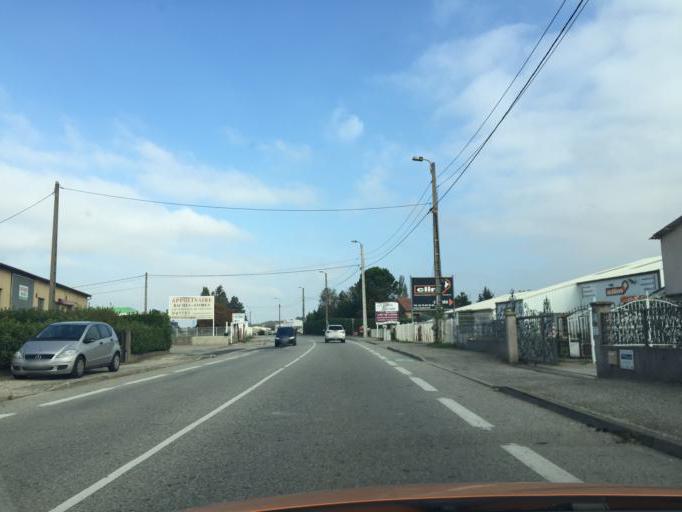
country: FR
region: Rhone-Alpes
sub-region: Departement de la Drome
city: Portes-les-Valence
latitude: 44.8809
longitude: 4.8870
